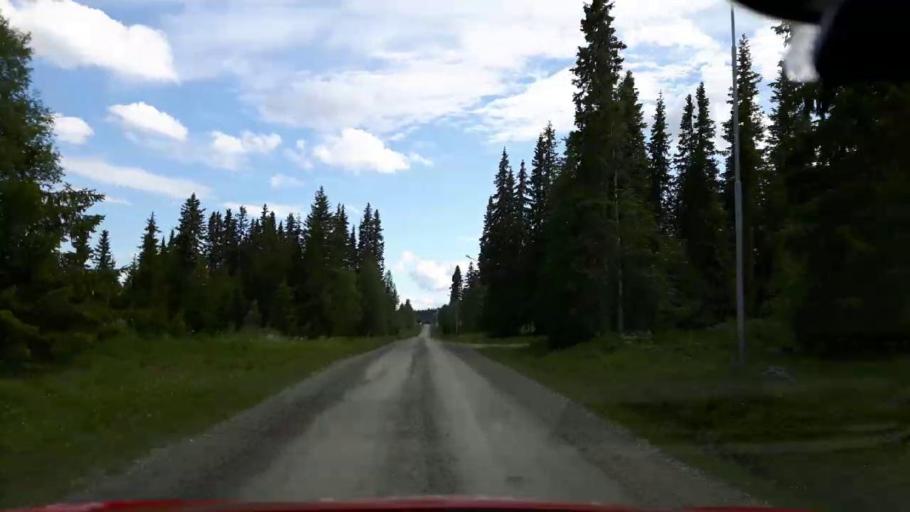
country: SE
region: Jaemtland
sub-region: Krokoms Kommun
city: Valla
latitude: 63.8329
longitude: 14.0401
